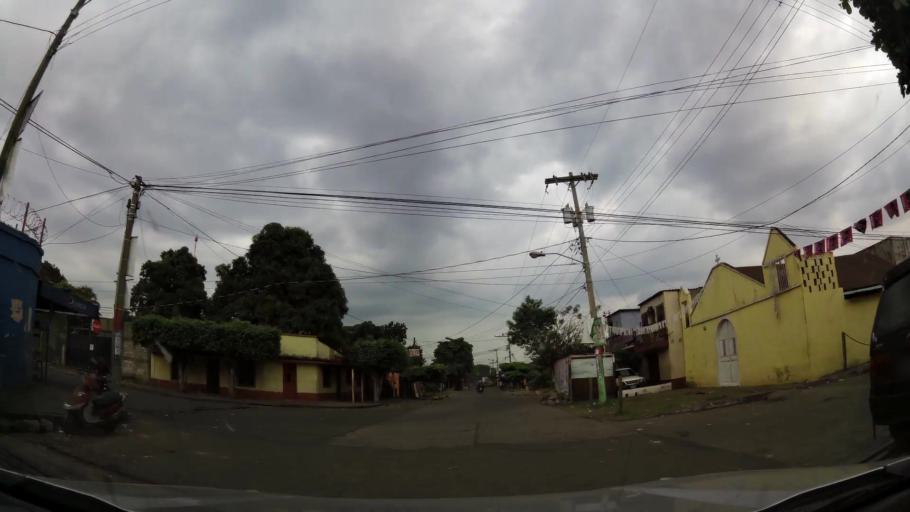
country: GT
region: Escuintla
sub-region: Municipio de Escuintla
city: Escuintla
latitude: 14.2882
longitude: -90.7815
